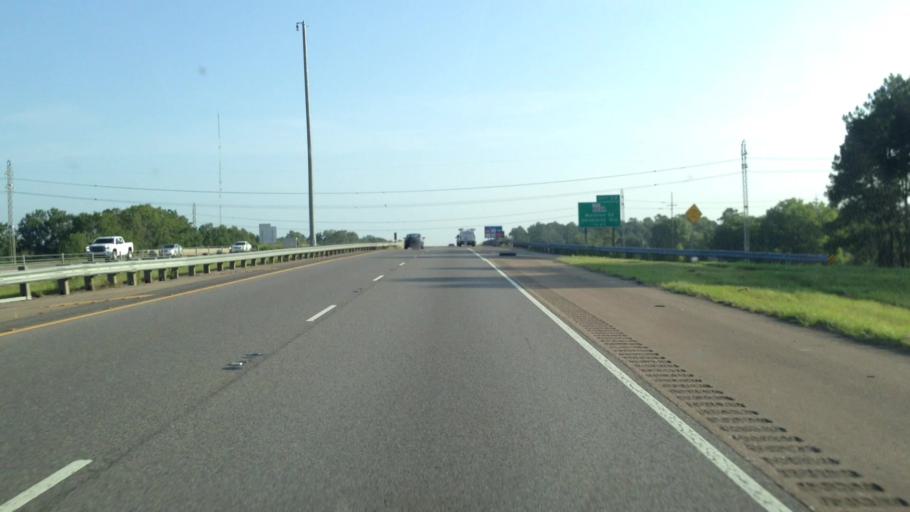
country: US
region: Louisiana
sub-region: Tangipahoa Parish
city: Hammond
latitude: 30.5030
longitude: -90.5035
